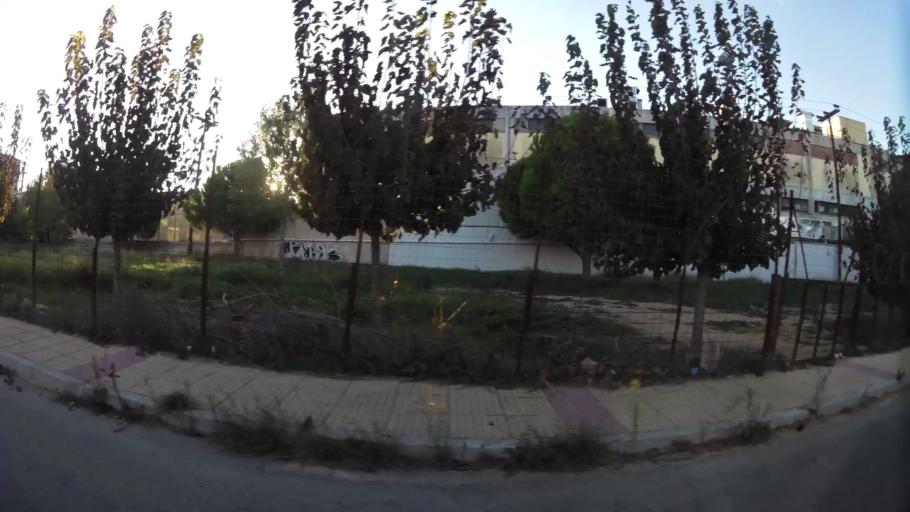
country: GR
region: Attica
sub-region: Nomarchia Athinas
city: Lykovrysi
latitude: 38.0711
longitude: 23.7883
